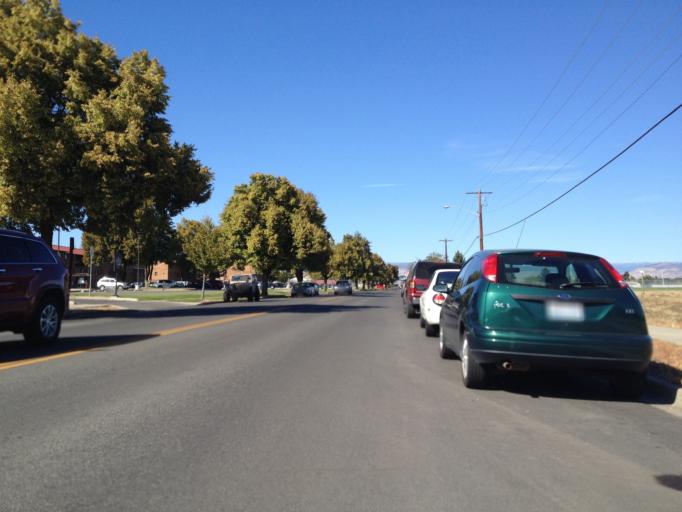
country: US
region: Washington
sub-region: Kittitas County
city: Ellensburg
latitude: 47.0071
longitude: -120.5319
